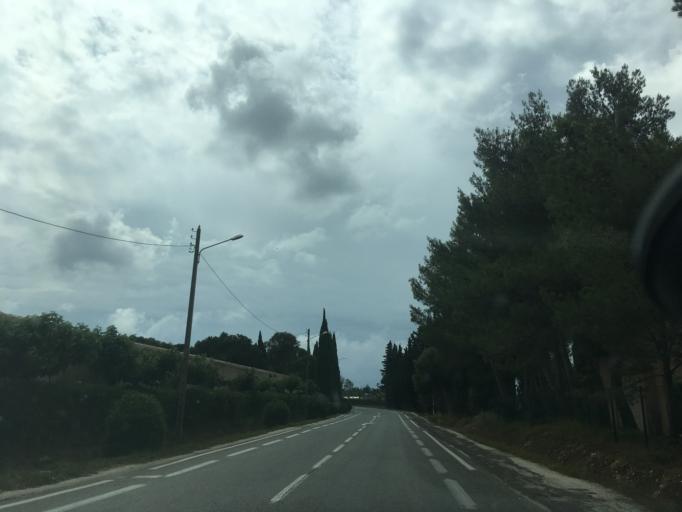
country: FR
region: Provence-Alpes-Cote d'Azur
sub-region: Departement du Var
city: La Londe-les-Maures
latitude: 43.1303
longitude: 6.2398
